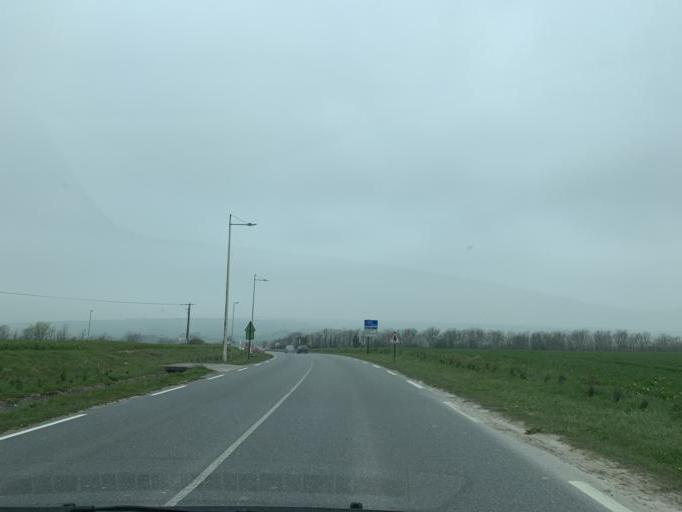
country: FR
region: Nord-Pas-de-Calais
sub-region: Departement du Pas-de-Calais
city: Marquise
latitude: 50.8268
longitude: 1.7040
